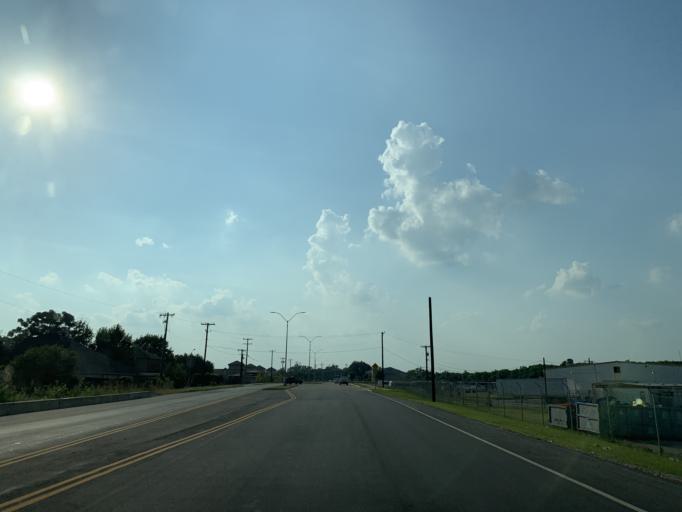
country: US
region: Texas
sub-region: Tarrant County
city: Hurst
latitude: 32.7996
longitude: -97.1793
